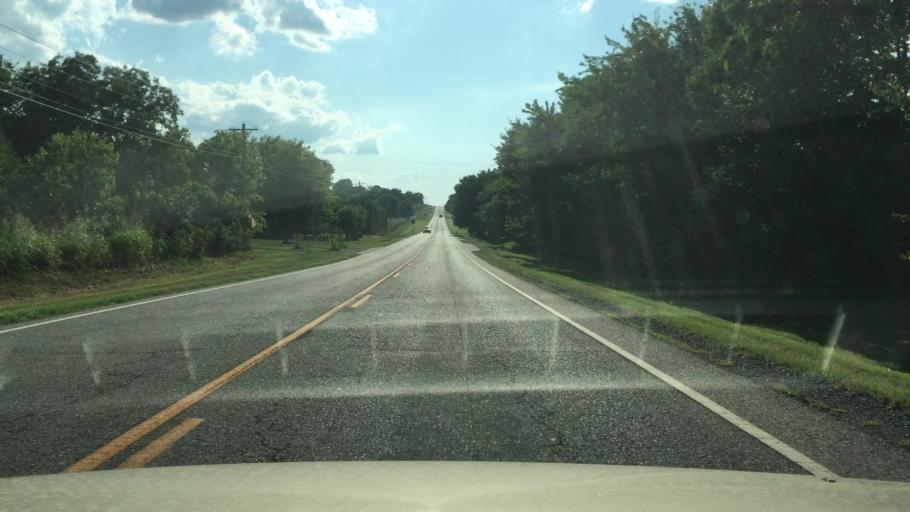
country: US
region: Oklahoma
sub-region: Cherokee County
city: Tahlequah
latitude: 35.9153
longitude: -95.0667
